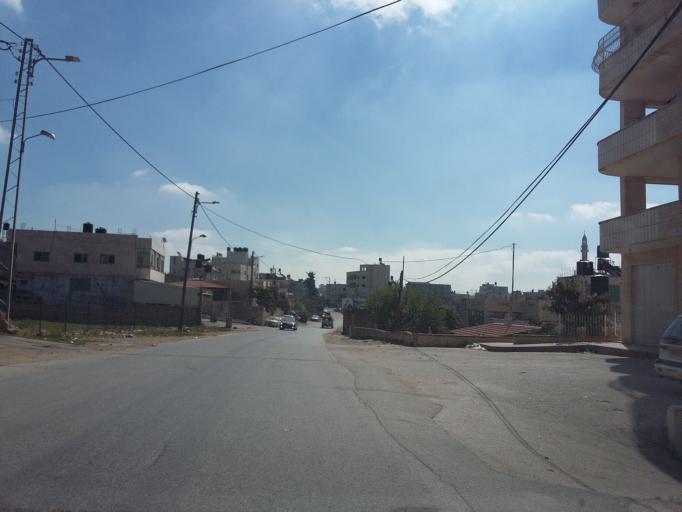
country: PS
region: West Bank
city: Al Jib
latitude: 31.8537
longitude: 35.1817
